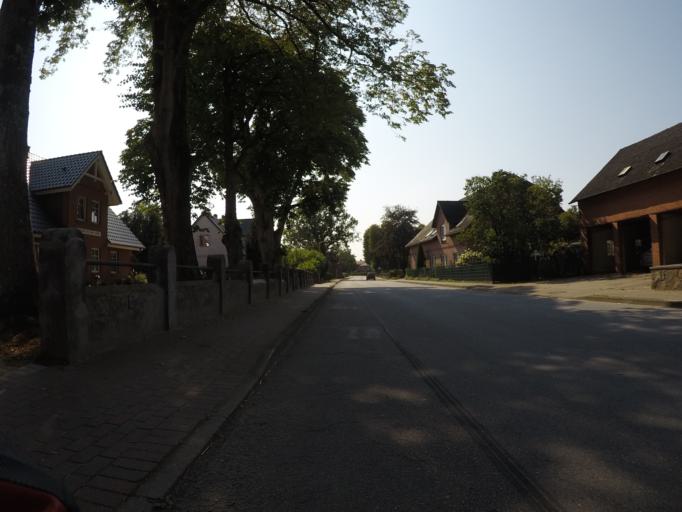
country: DE
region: Schleswig-Holstein
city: Todesfelde
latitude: 53.8959
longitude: 10.1797
